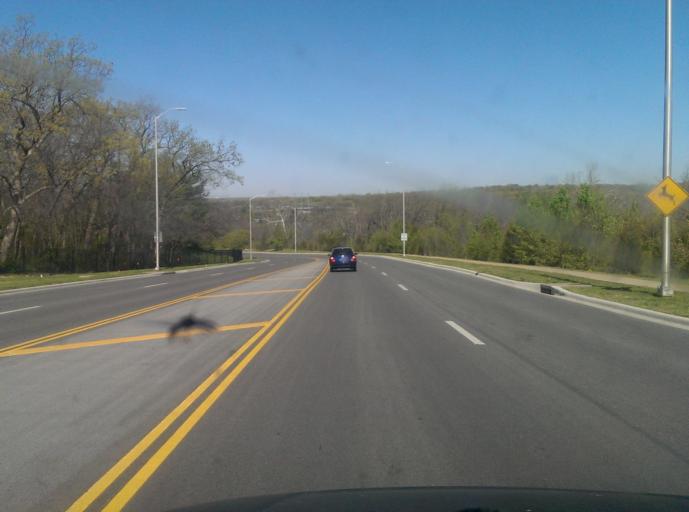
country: US
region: Kansas
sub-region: Johnson County
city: Leawood
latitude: 38.9302
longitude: -94.6105
